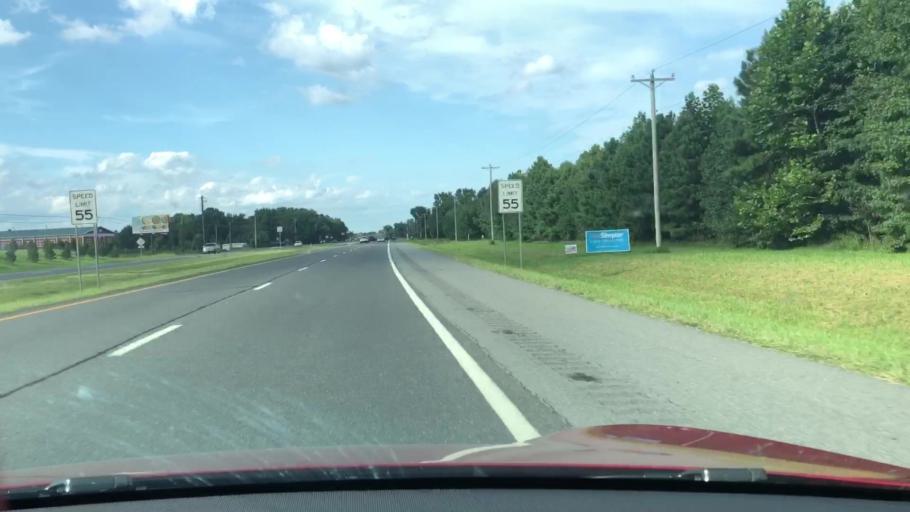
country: US
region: Delaware
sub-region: Kent County
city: Harrington
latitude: 38.8575
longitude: -75.5785
